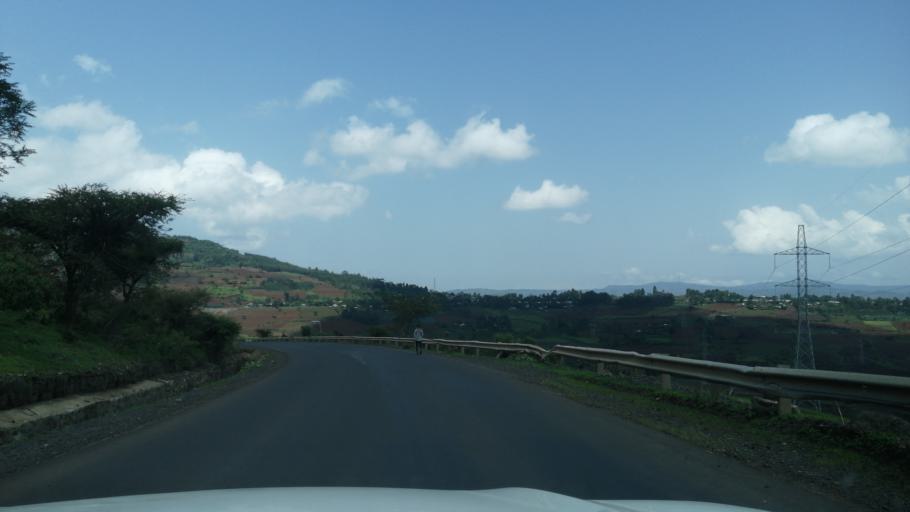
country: ET
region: Oromiya
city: Guder
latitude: 8.9878
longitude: 37.6081
